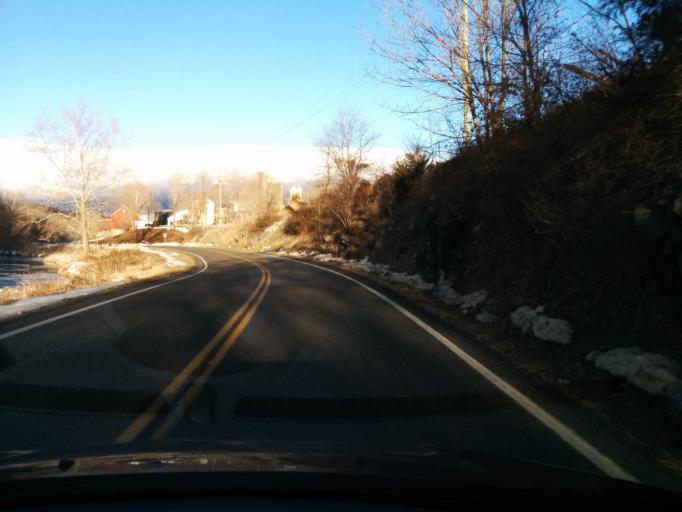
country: US
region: Virginia
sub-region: City of Lexington
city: Lexington
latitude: 37.7456
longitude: -79.5126
